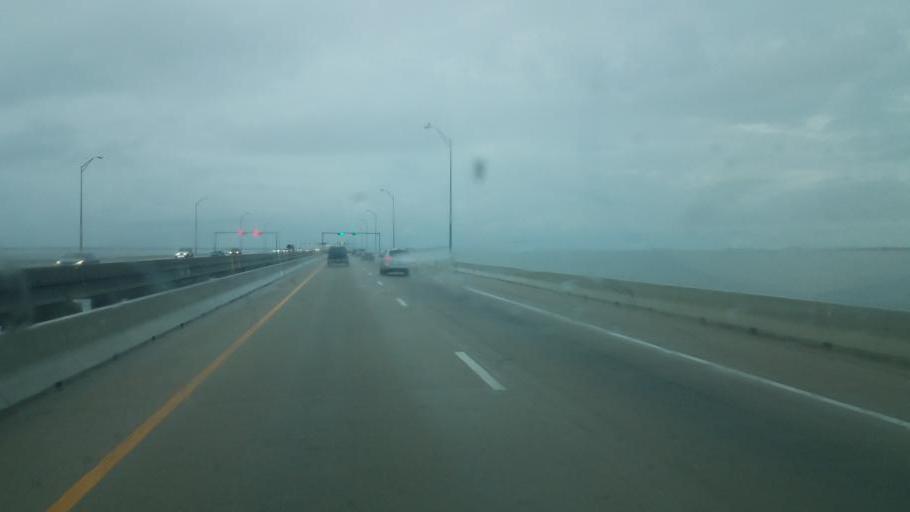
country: US
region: Virginia
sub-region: City of Newport News
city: Newport News
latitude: 36.9089
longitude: -76.4192
